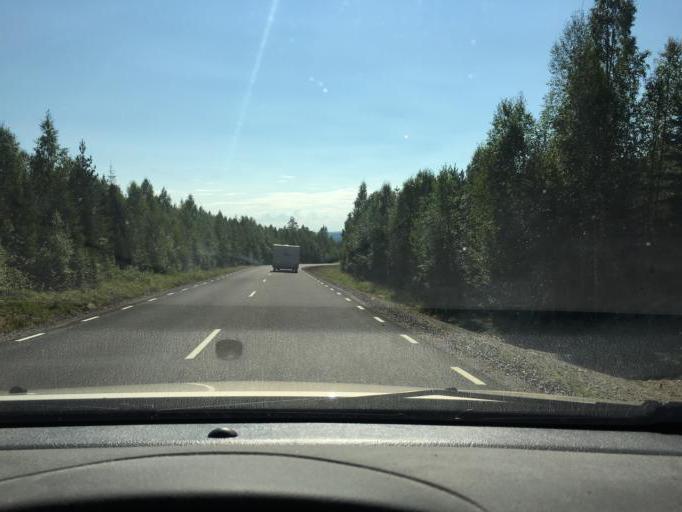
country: SE
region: Norrbotten
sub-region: Lulea Kommun
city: Ranea
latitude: 66.0513
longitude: 22.2126
